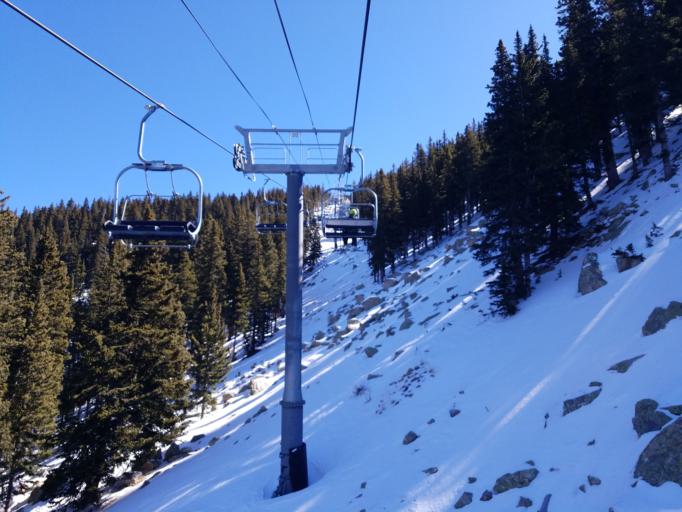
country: US
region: New Mexico
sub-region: Santa Fe County
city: Santa Fe
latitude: 35.7923
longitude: -105.7812
